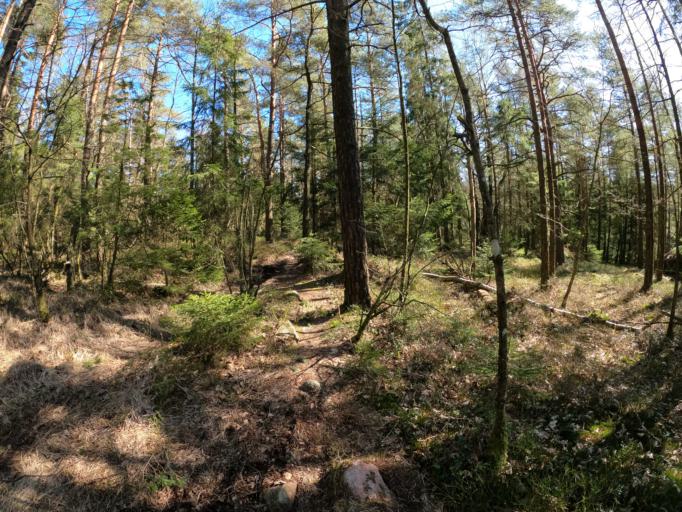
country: SE
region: Vaestra Goetaland
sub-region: Harryda Kommun
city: Molnlycke
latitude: 57.6255
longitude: 12.1224
